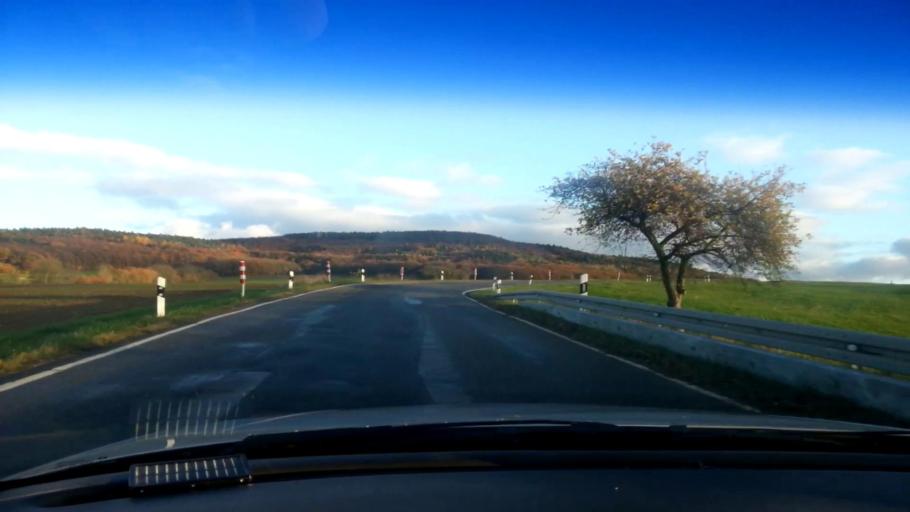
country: DE
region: Bavaria
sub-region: Upper Franconia
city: Hirschaid
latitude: 49.8534
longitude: 11.0167
